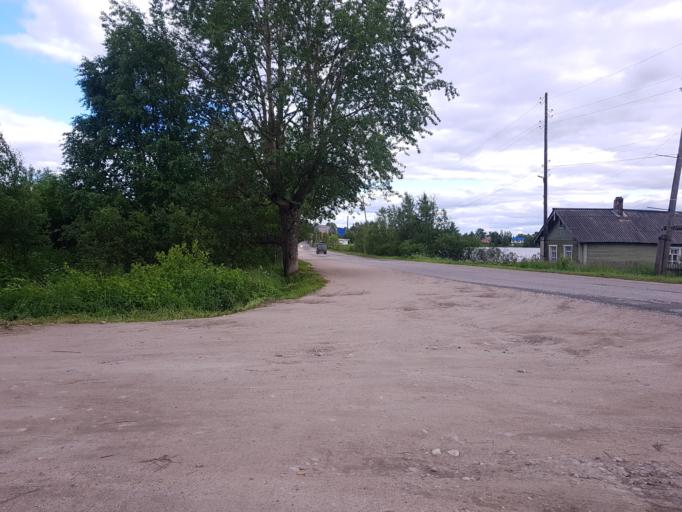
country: RU
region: Republic of Karelia
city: Kalevala
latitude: 65.2008
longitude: 31.1772
